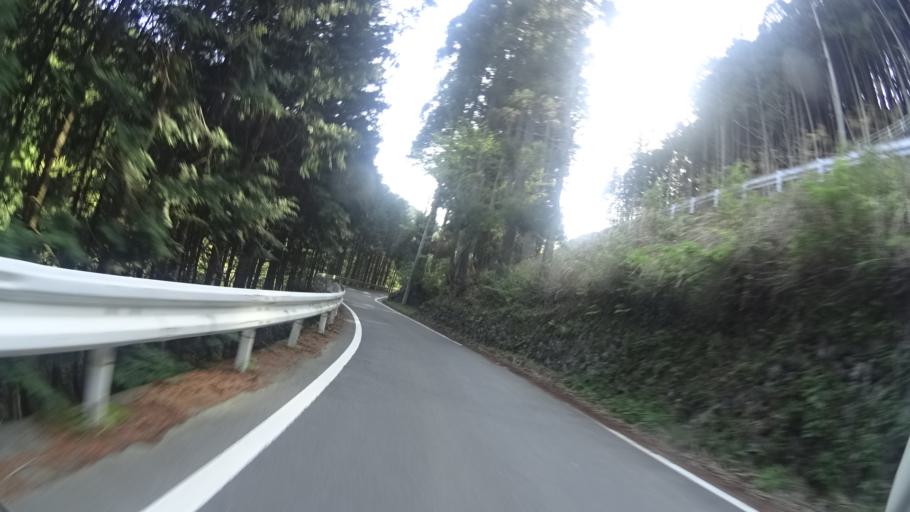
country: JP
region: Tokushima
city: Ikedacho
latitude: 33.8671
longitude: 133.9651
